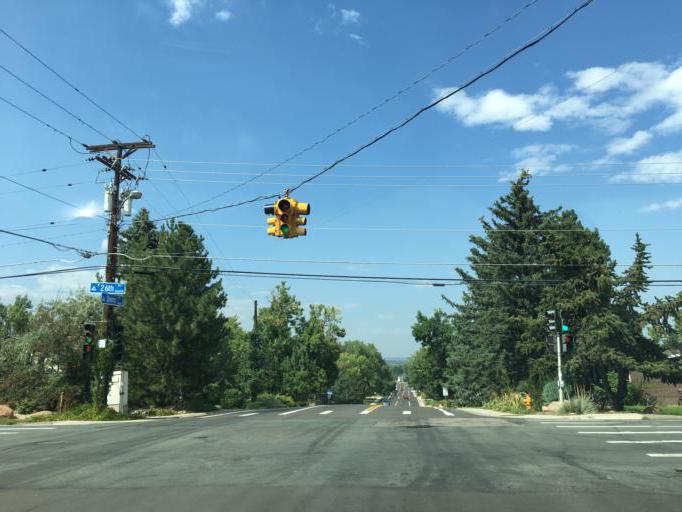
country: US
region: Colorado
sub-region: Jefferson County
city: Applewood
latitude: 39.7541
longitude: -105.1284
